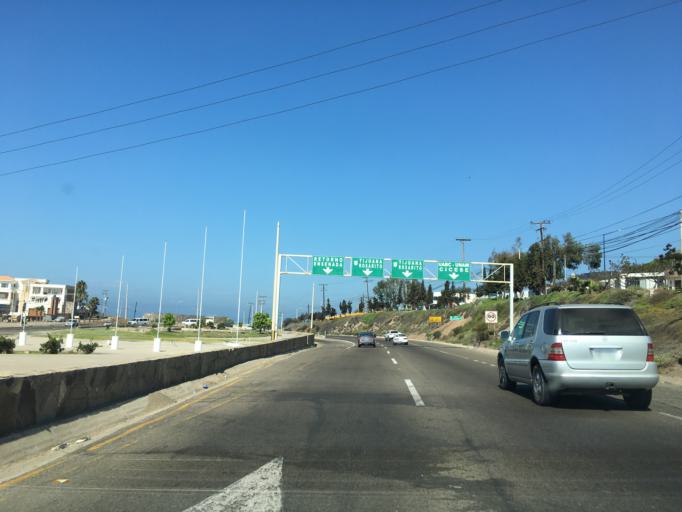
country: MX
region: Baja California
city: El Sauzal
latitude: 31.8673
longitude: -116.6632
